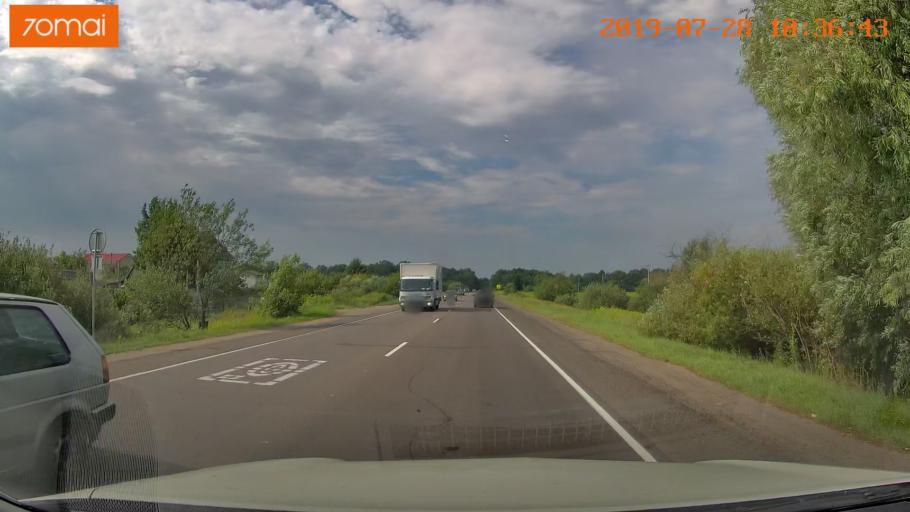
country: RU
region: Kaliningrad
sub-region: Gorod Kaliningrad
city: Kaliningrad
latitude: 54.7363
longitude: 20.4184
